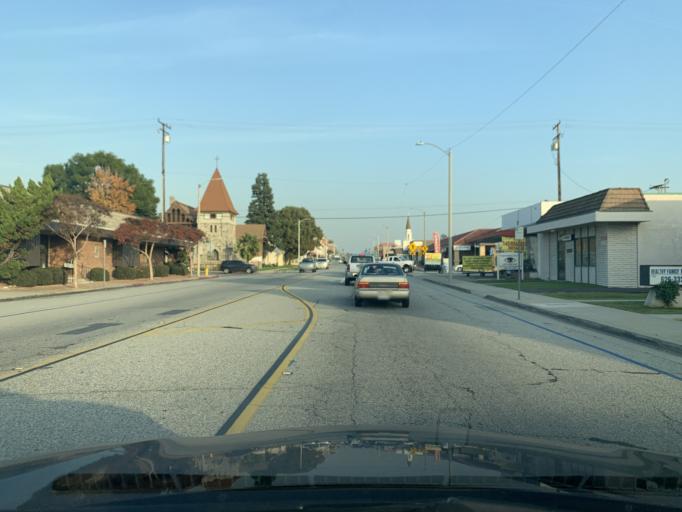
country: US
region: California
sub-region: Los Angeles County
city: Covina
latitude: 34.0863
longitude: -117.8931
